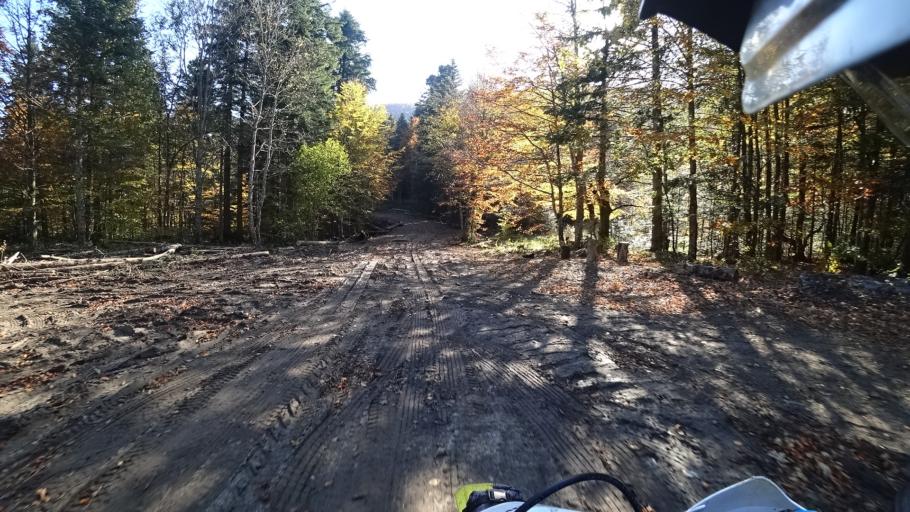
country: HR
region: Karlovacka
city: Plaski
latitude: 45.0219
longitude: 15.3753
